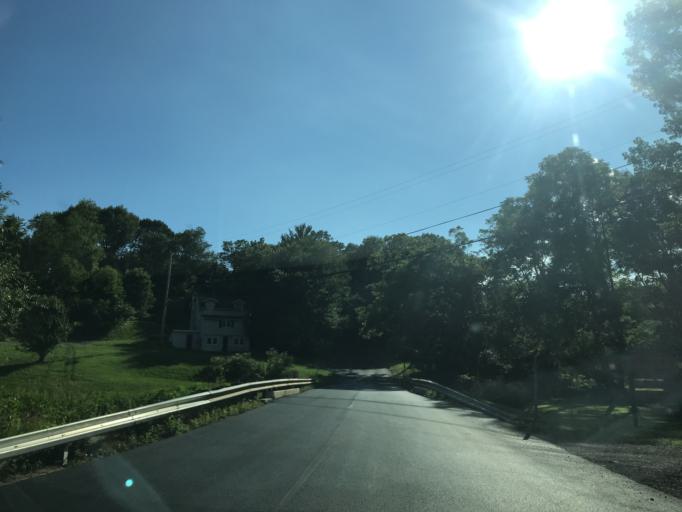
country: US
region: Maryland
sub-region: Carroll County
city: Hampstead
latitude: 39.6359
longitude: -76.8156
